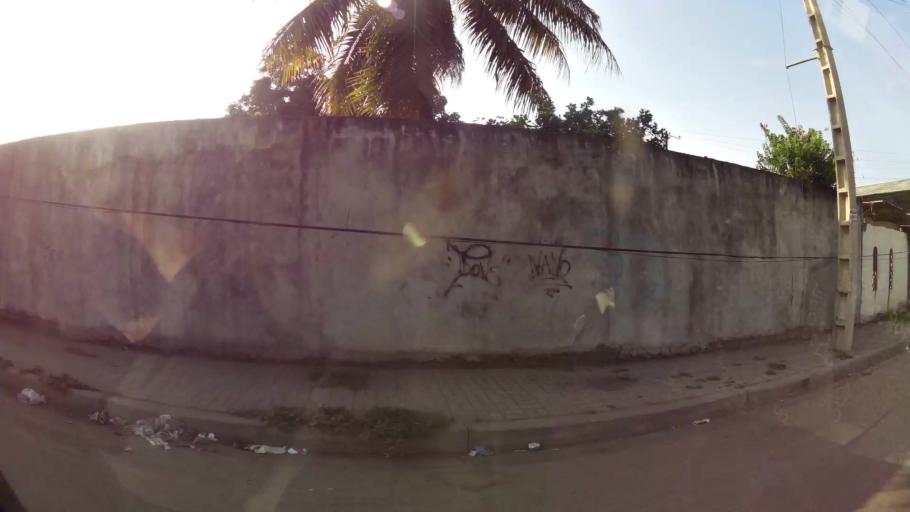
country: EC
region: Guayas
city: Eloy Alfaro
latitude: -2.1821
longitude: -79.8358
